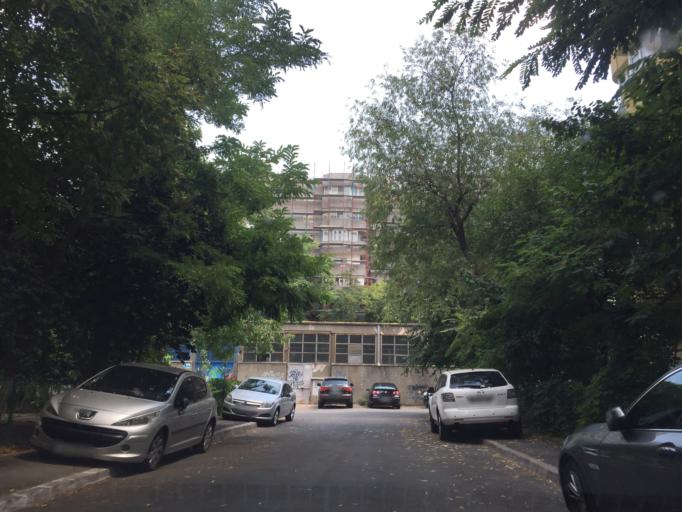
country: RO
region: Bucuresti
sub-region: Municipiul Bucuresti
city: Bucharest
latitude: 44.4208
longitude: 26.1191
